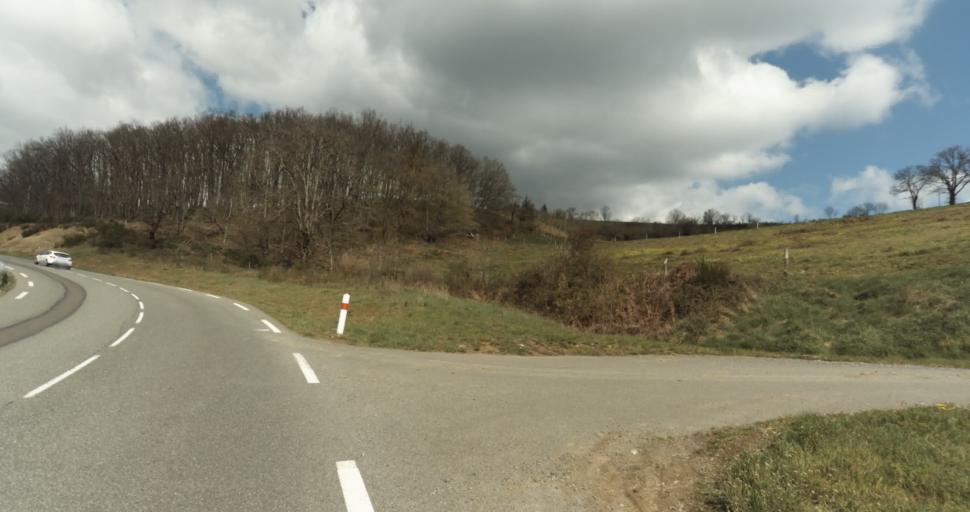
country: FR
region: Rhone-Alpes
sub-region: Departement du Rhone
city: Tarare
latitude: 45.9288
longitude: 4.3986
